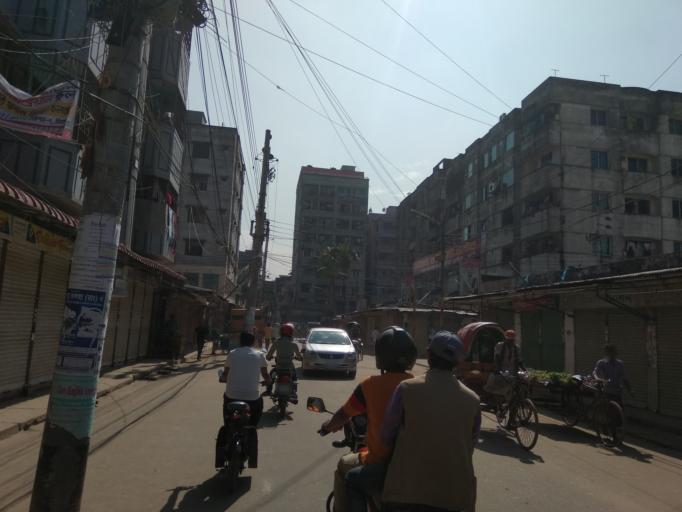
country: BD
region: Dhaka
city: Tungi
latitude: 23.8175
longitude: 90.3673
